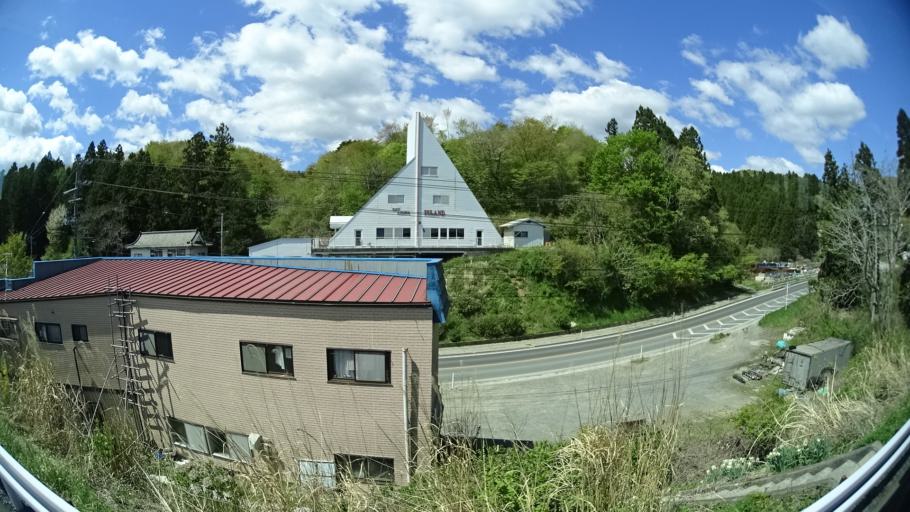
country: JP
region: Miyagi
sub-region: Oshika Gun
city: Onagawa Cho
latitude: 38.6635
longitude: 141.4455
